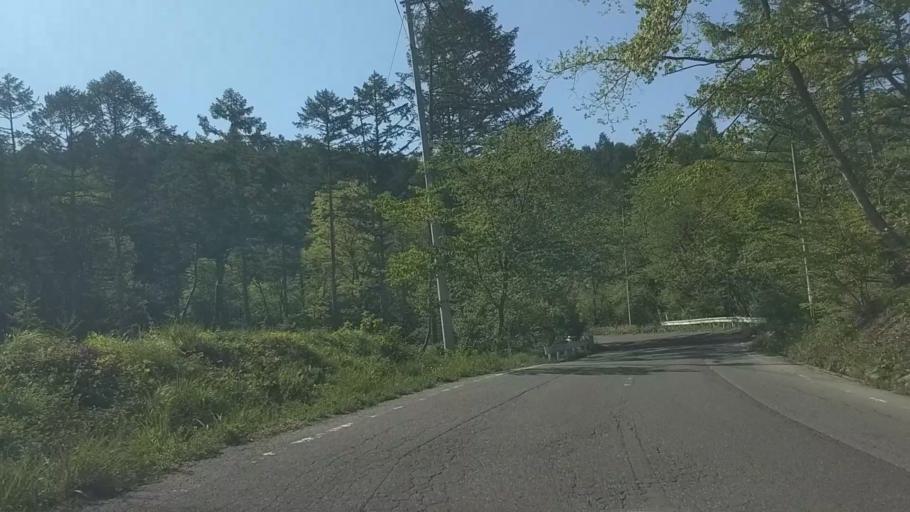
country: JP
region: Yamanashi
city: Nirasaki
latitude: 35.8947
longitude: 138.4064
